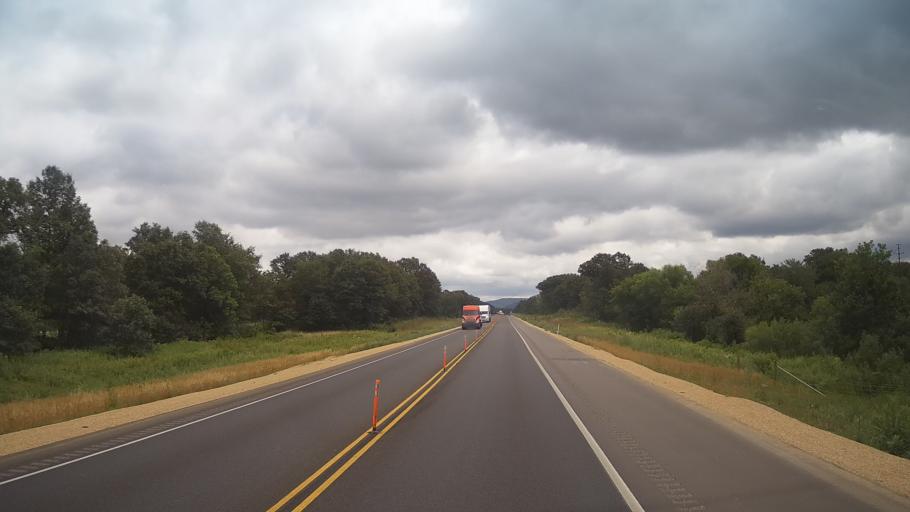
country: US
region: Wisconsin
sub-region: Monroe County
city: Sparta
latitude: 43.9430
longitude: -90.7090
